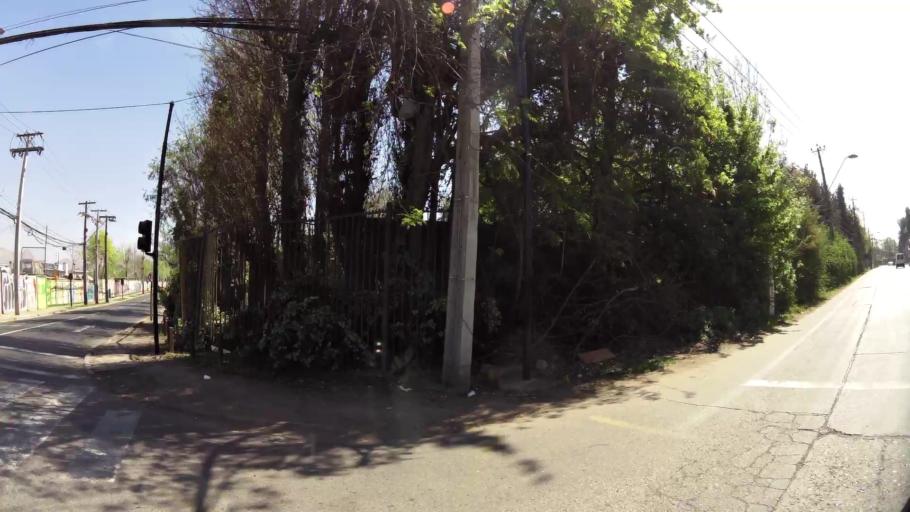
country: CL
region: Santiago Metropolitan
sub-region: Provincia de Santiago
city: Lo Prado
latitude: -33.3677
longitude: -70.7056
